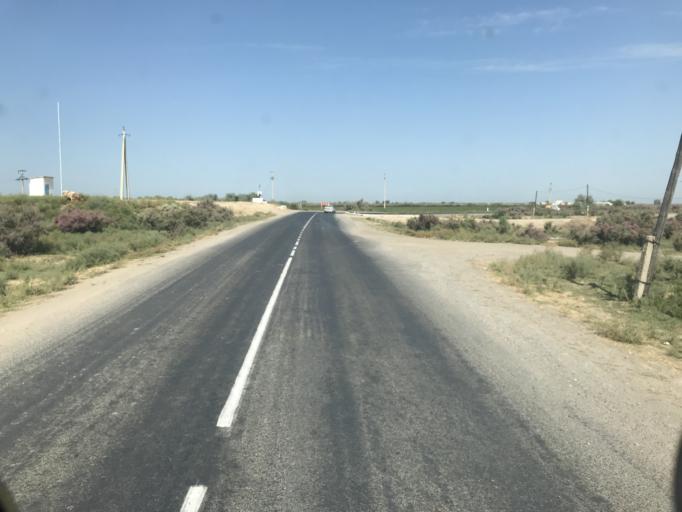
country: KZ
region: Ongtustik Qazaqstan
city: Myrzakent
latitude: 40.6795
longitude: 68.5332
